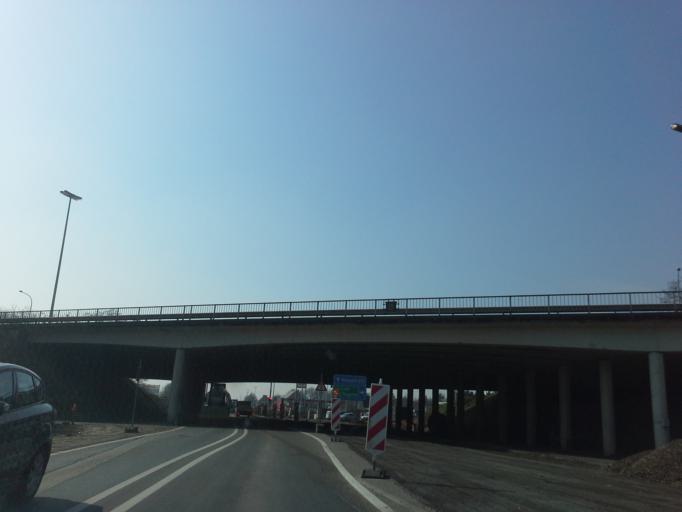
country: BE
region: Flanders
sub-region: Provincie Limburg
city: Hoeselt
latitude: 50.8590
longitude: 5.5004
